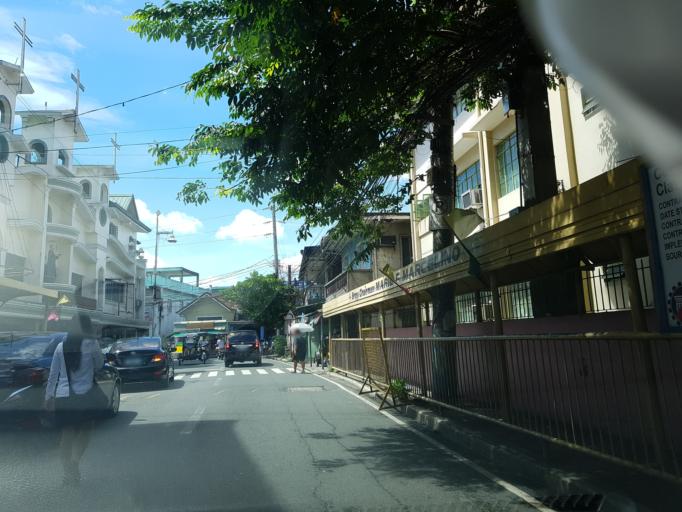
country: PH
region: Calabarzon
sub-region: Province of Rizal
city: Pateros
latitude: 14.5345
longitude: 121.0676
